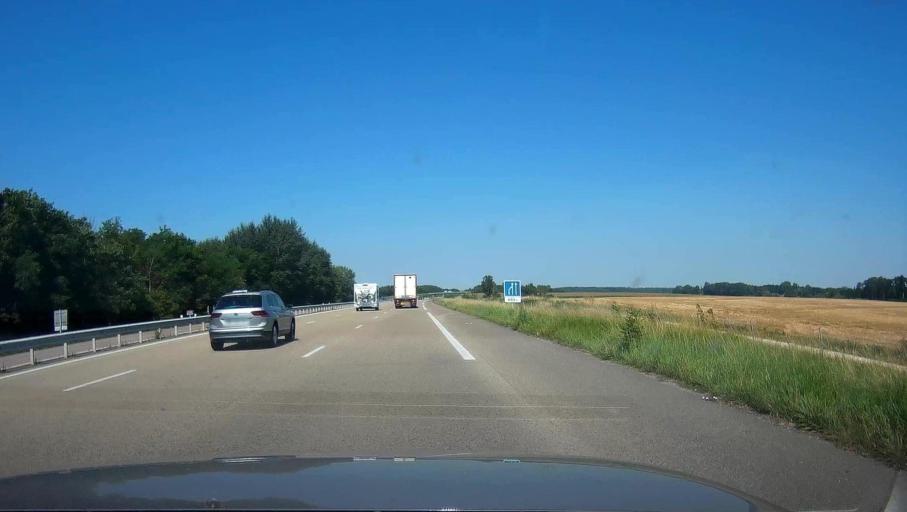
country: FR
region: Champagne-Ardenne
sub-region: Departement de l'Aube
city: Verrieres
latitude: 48.2345
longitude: 4.1756
